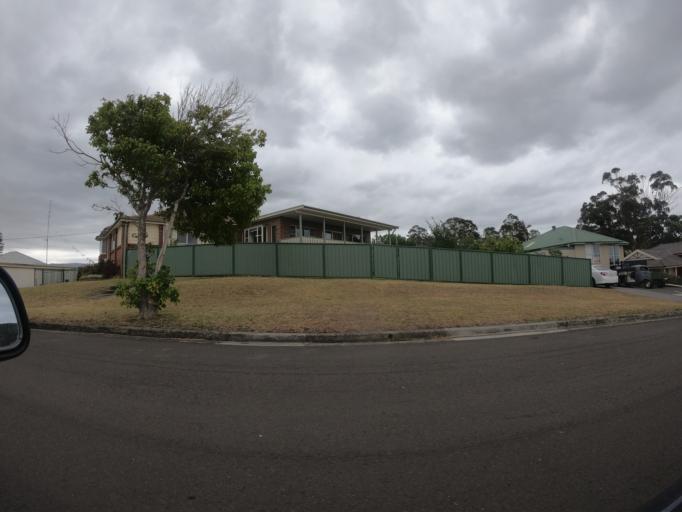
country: AU
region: New South Wales
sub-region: Wollongong
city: Berkeley
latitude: -34.4790
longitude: 150.8436
